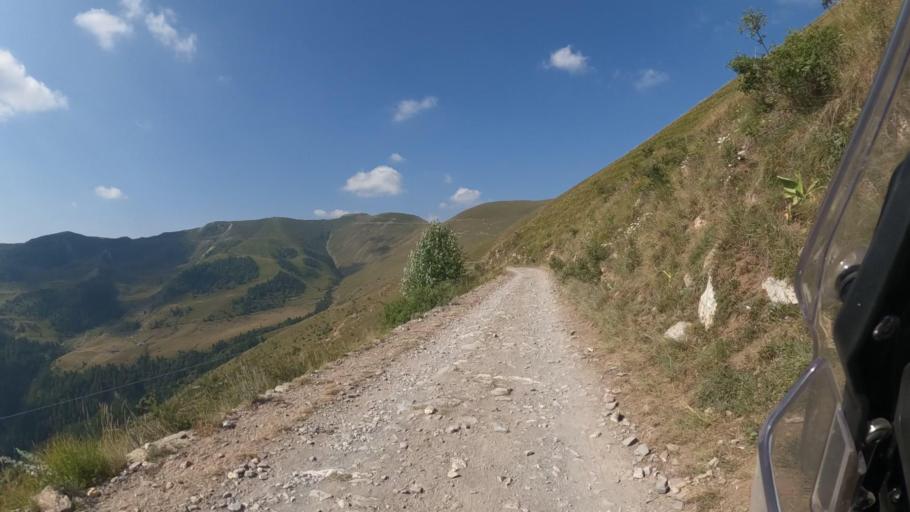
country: IT
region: Piedmont
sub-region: Provincia di Cuneo
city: Briga Alta
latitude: 44.0831
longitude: 7.7316
